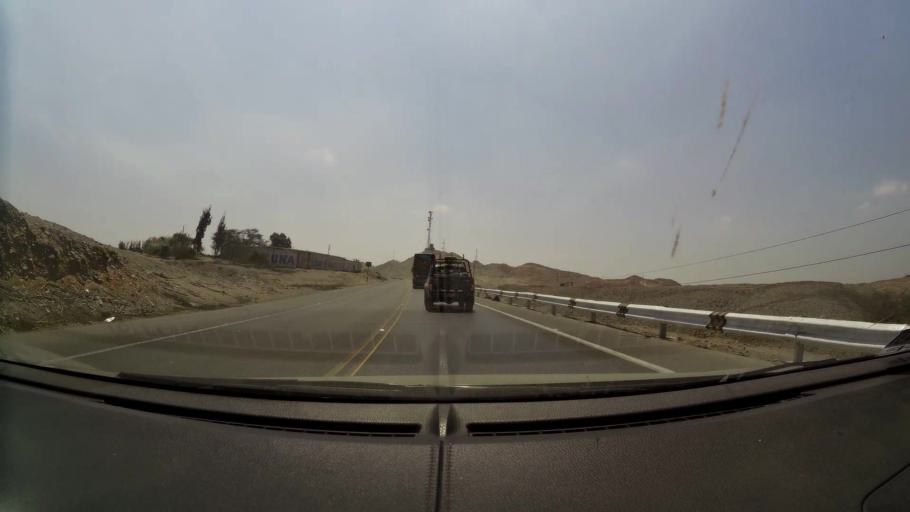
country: PE
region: La Libertad
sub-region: Provincia de Pacasmayo
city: Pacasmayo
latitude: -7.3914
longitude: -79.5549
